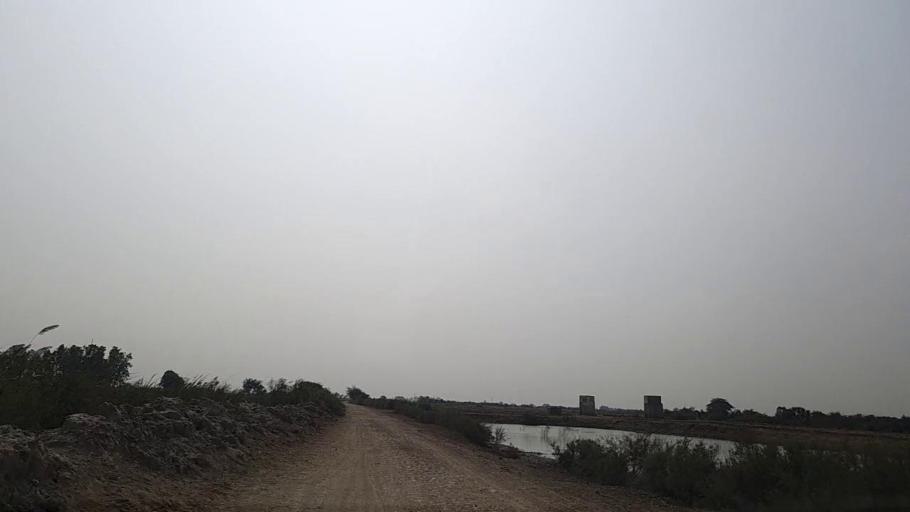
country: PK
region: Sindh
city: Mirpur Sakro
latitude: 24.6360
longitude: 67.7670
